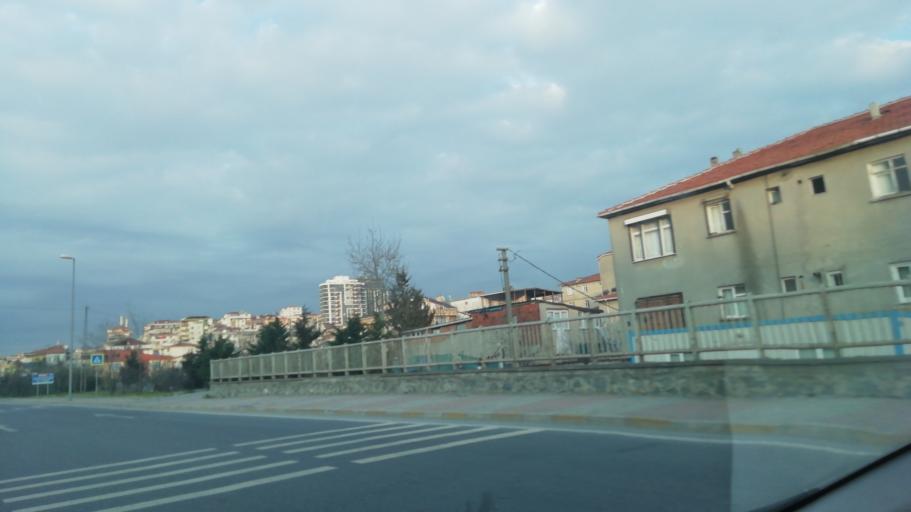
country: TR
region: Istanbul
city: Mahmutbey
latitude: 41.0140
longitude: 28.7742
